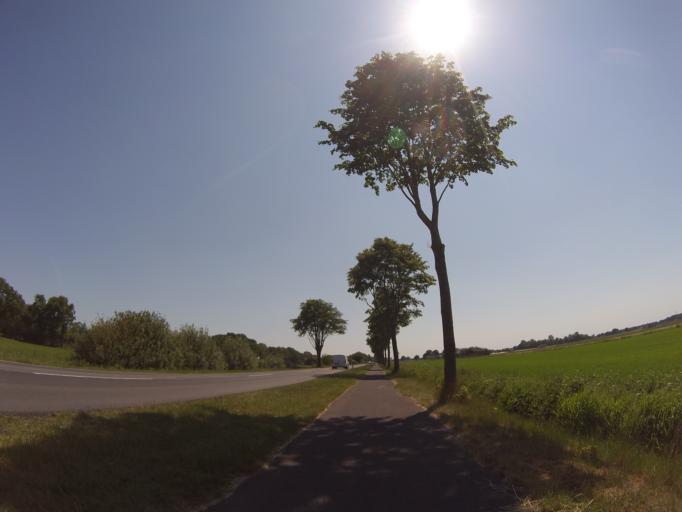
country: NL
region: Drenthe
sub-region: Gemeente Emmen
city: Schoonebeek
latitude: 52.6499
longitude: 6.8704
